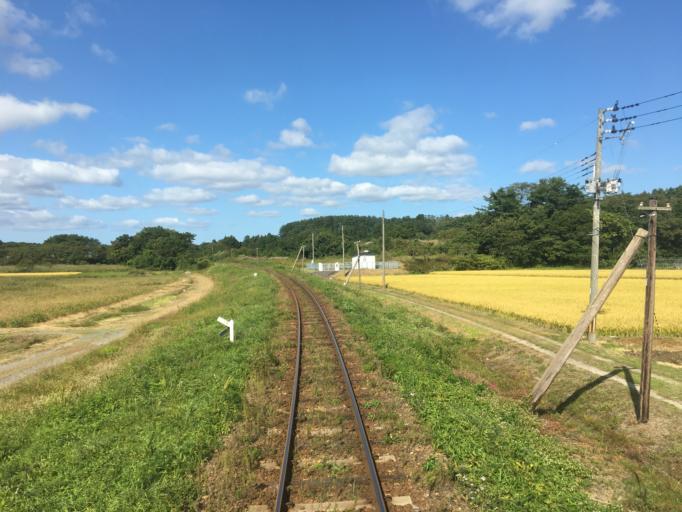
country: JP
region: Aomori
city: Goshogawara
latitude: 40.9532
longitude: 140.4430
